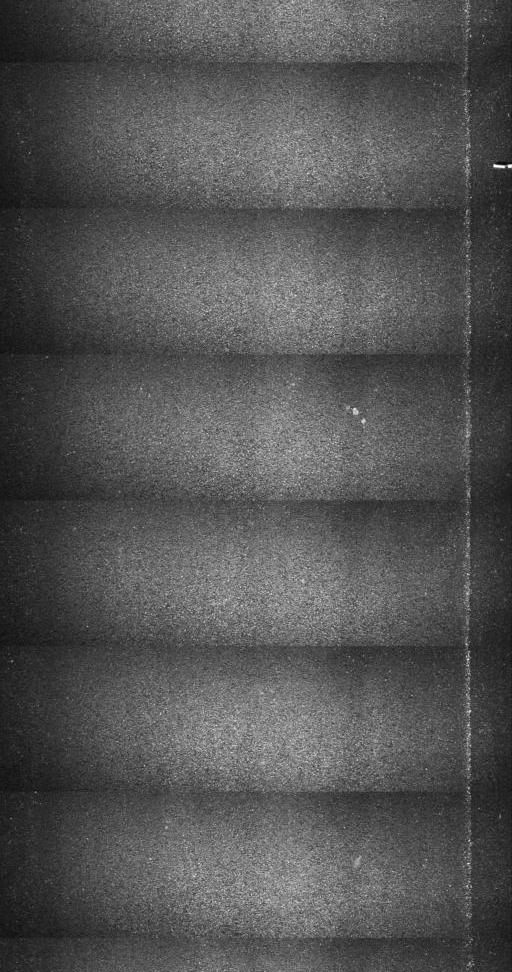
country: US
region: Vermont
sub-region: Franklin County
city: Richford
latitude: 44.8352
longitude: -72.6087
